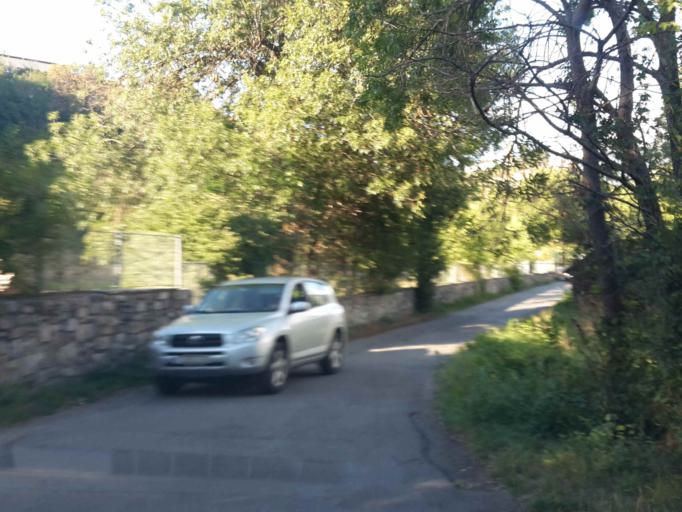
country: FR
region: Provence-Alpes-Cote d'Azur
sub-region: Departement des Hautes-Alpes
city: Embrun
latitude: 44.5577
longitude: 6.4873
